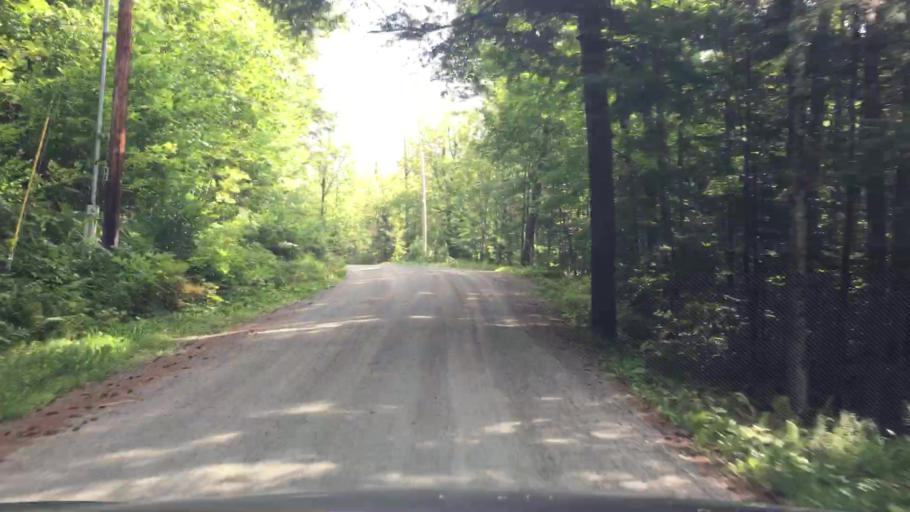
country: US
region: New Hampshire
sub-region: Grafton County
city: Littleton
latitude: 44.3062
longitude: -71.8932
